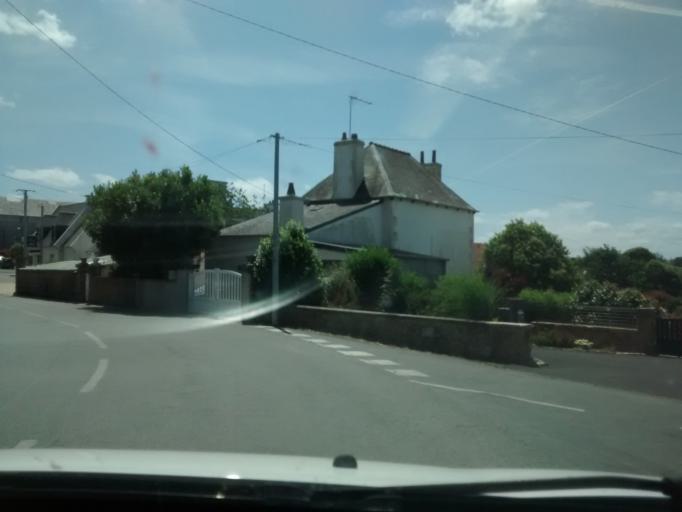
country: FR
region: Brittany
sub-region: Departement des Cotes-d'Armor
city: Trelevern
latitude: 48.8139
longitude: -3.3588
